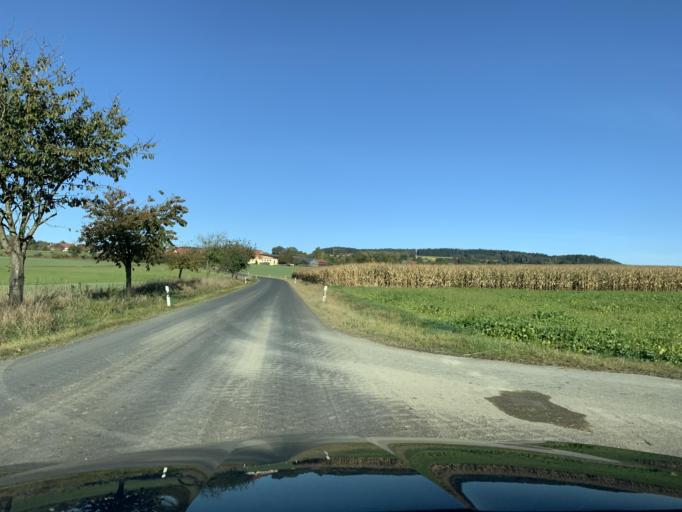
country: DE
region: Bavaria
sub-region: Upper Palatinate
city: Thanstein
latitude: 49.3994
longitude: 12.4677
